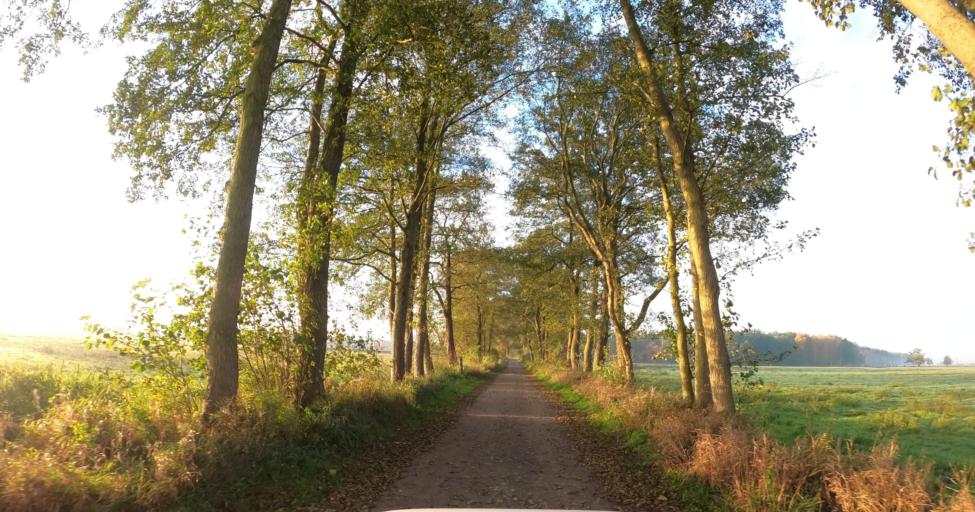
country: PL
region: West Pomeranian Voivodeship
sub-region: Powiat goleniowski
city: Goleniow
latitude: 53.5690
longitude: 14.7608
